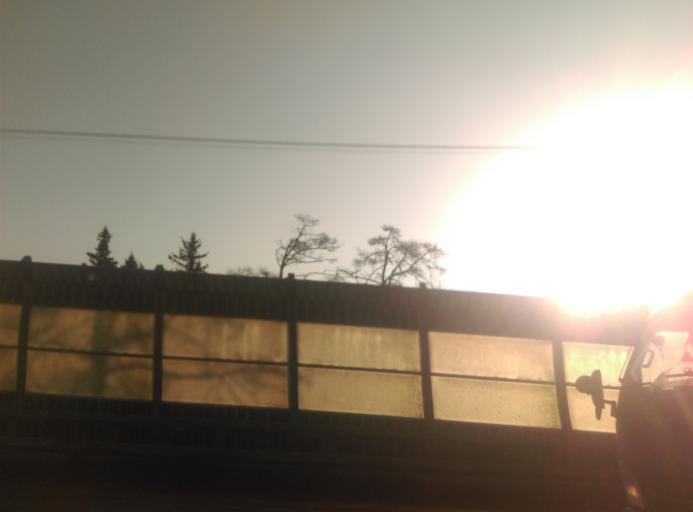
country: RU
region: Moskovskaya
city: Vidnoye
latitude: 55.5542
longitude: 37.6831
